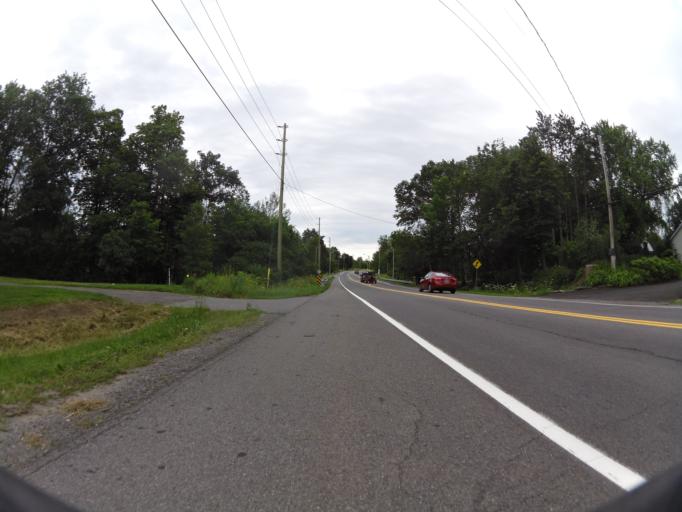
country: CA
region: Ontario
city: Bells Corners
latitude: 45.2443
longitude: -75.7071
